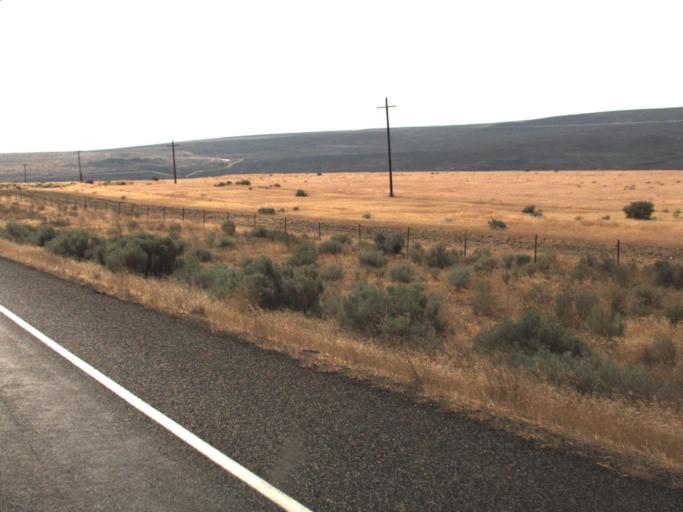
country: US
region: Washington
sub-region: Grant County
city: Desert Aire
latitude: 46.6280
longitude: -119.7267
